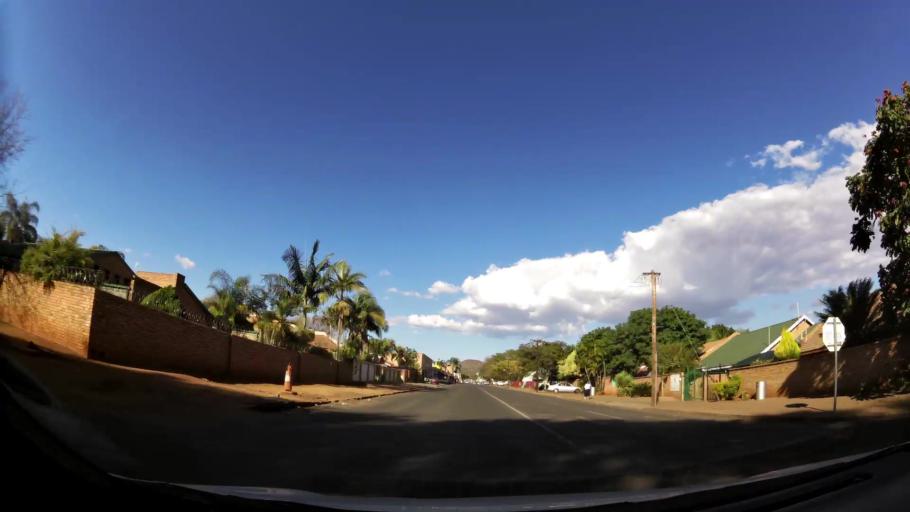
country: ZA
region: Limpopo
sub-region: Waterberg District Municipality
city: Mokopane
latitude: -24.1817
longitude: 29.0070
